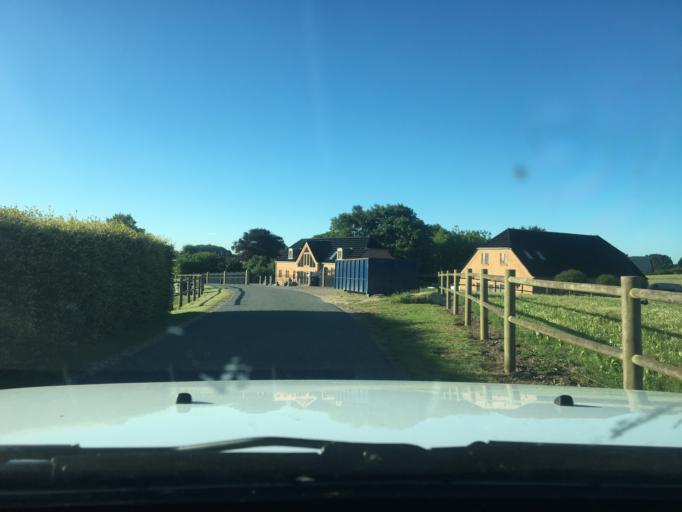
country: DK
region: Central Jutland
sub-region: Randers Kommune
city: Randers
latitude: 56.4035
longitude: 10.0612
